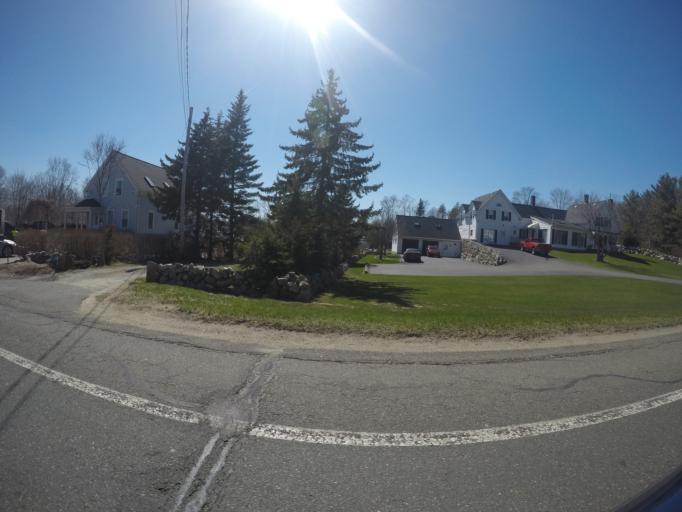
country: US
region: Massachusetts
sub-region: Norfolk County
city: Stoughton
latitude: 42.0850
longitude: -71.0910
